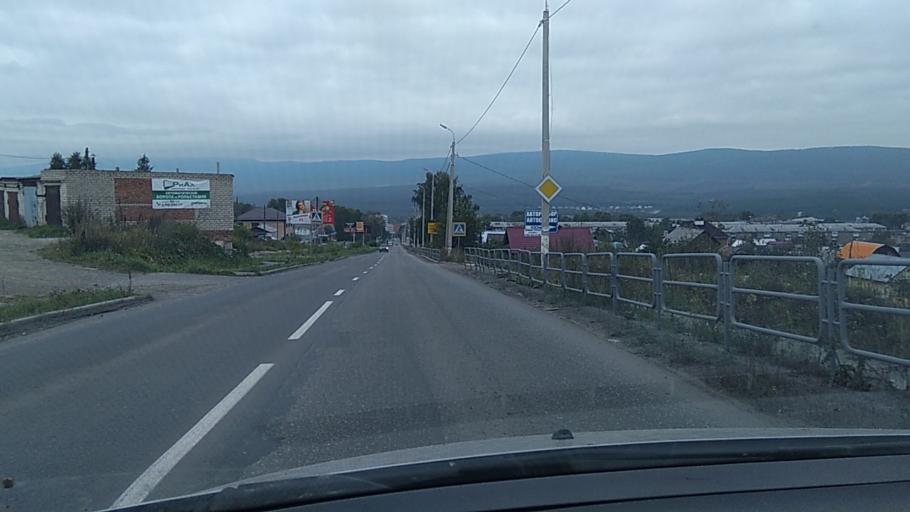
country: RU
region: Chelyabinsk
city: Zlatoust
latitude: 55.1160
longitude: 59.7316
